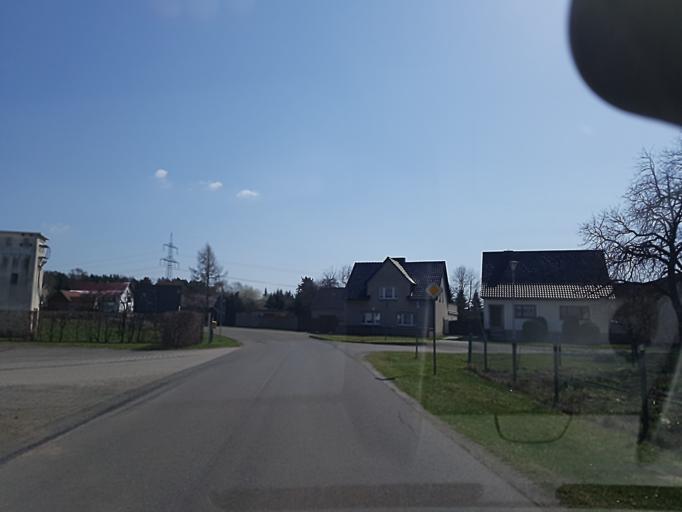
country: DE
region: Brandenburg
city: Schonborn
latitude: 51.5609
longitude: 13.4823
